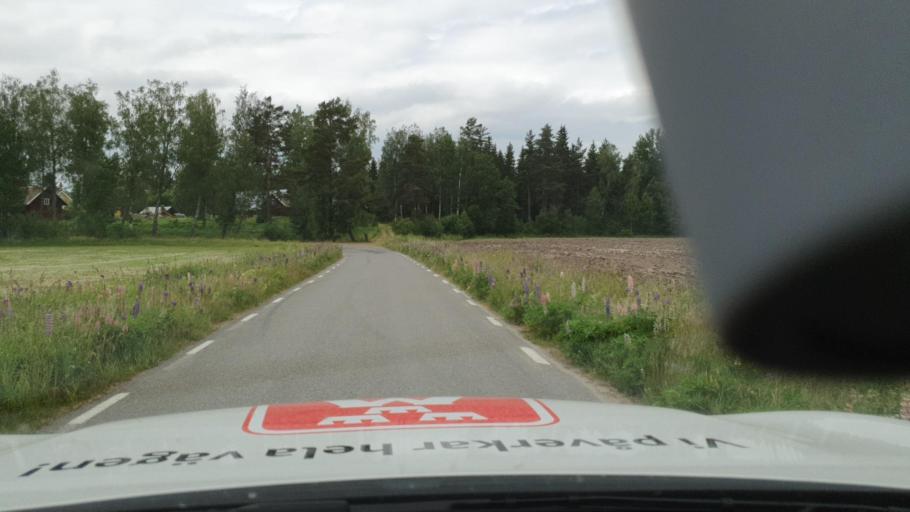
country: SE
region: Vaestra Goetaland
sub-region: Tidaholms Kommun
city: Tidaholm
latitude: 58.1650
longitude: 14.0289
